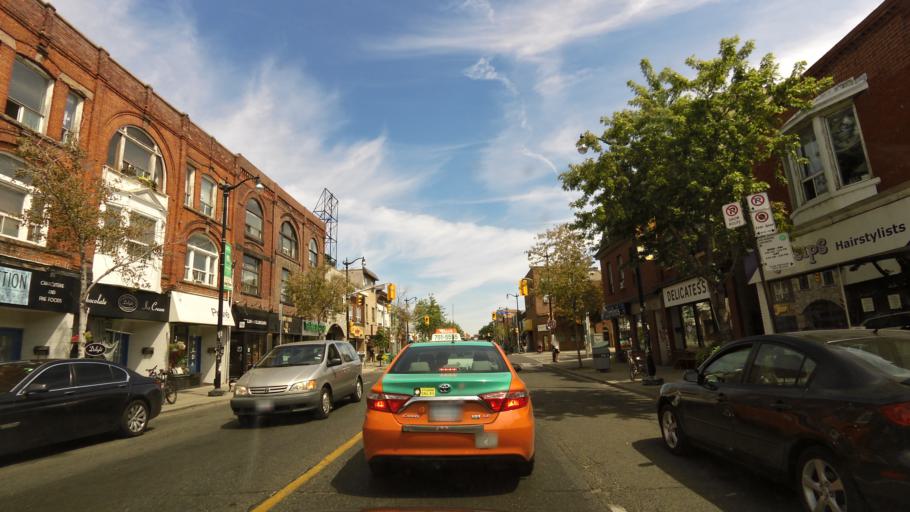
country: CA
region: Ontario
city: Toronto
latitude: 43.6655
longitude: -79.4708
